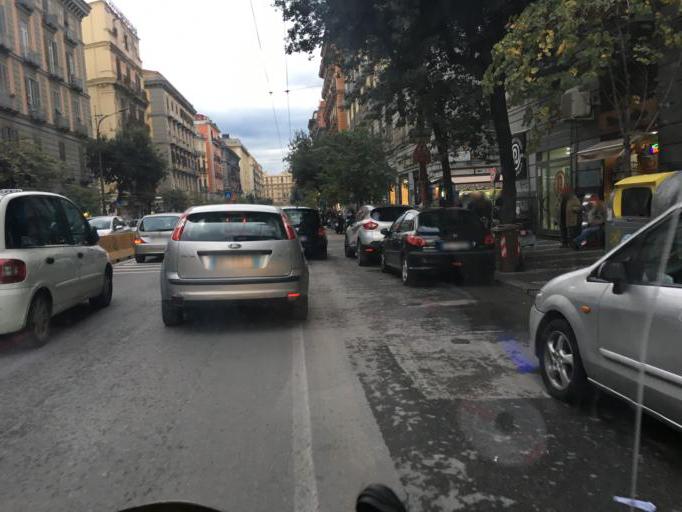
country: IT
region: Campania
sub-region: Provincia di Napoli
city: Napoli
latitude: 40.8468
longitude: 14.2603
